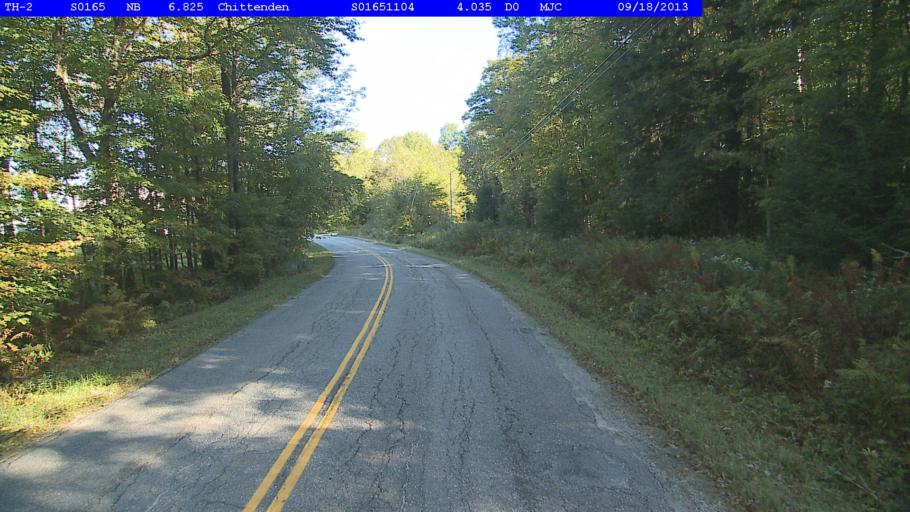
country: US
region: Vermont
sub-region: Rutland County
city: Rutland
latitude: 43.7322
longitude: -72.9709
